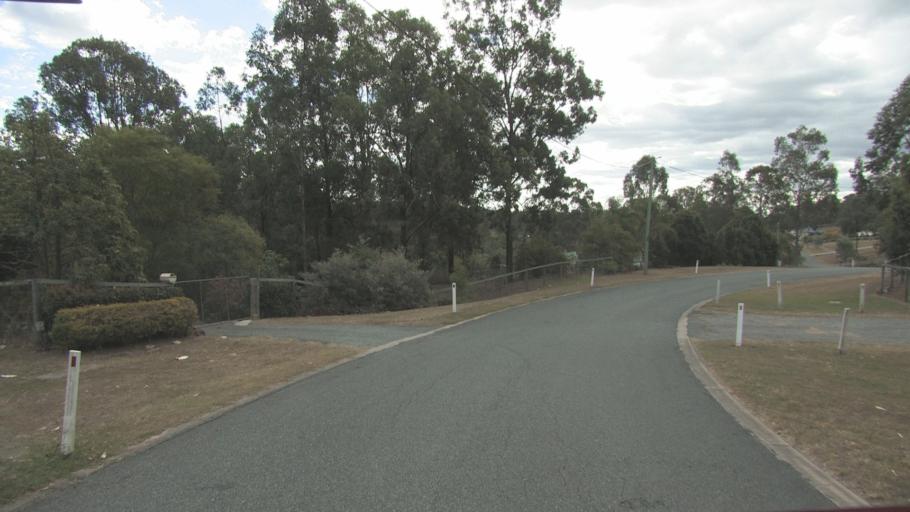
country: AU
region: Queensland
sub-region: Logan
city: Cedar Vale
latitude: -27.8860
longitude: 153.0133
